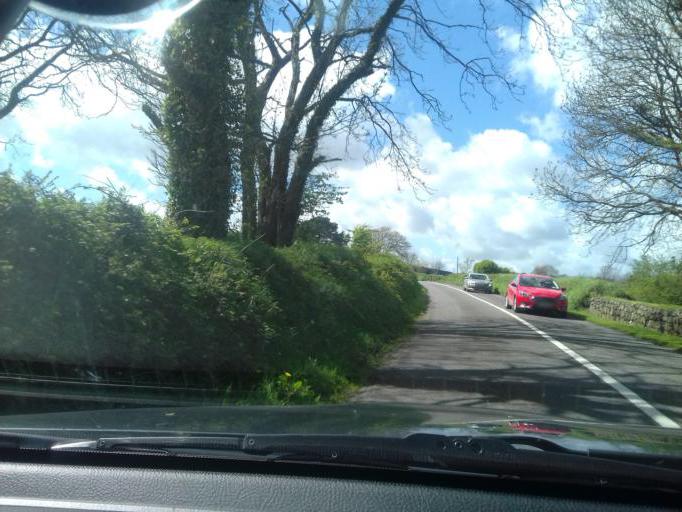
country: IE
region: Munster
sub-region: Waterford
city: Dunmore East
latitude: 52.2442
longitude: -6.9912
